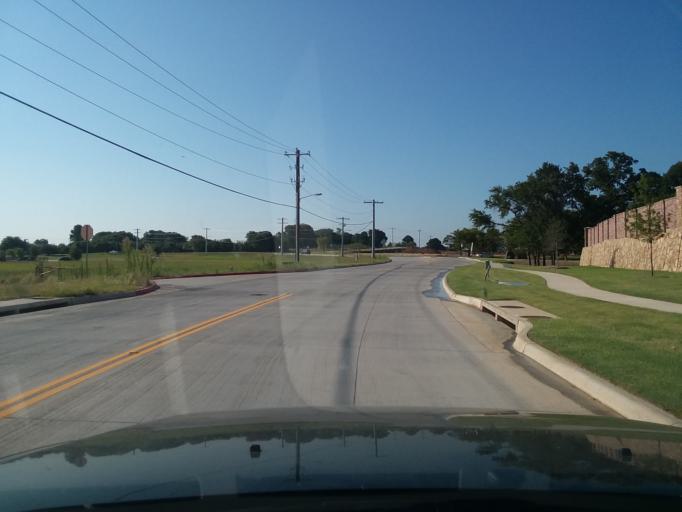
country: US
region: Texas
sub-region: Denton County
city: Double Oak
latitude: 33.0614
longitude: -97.0798
